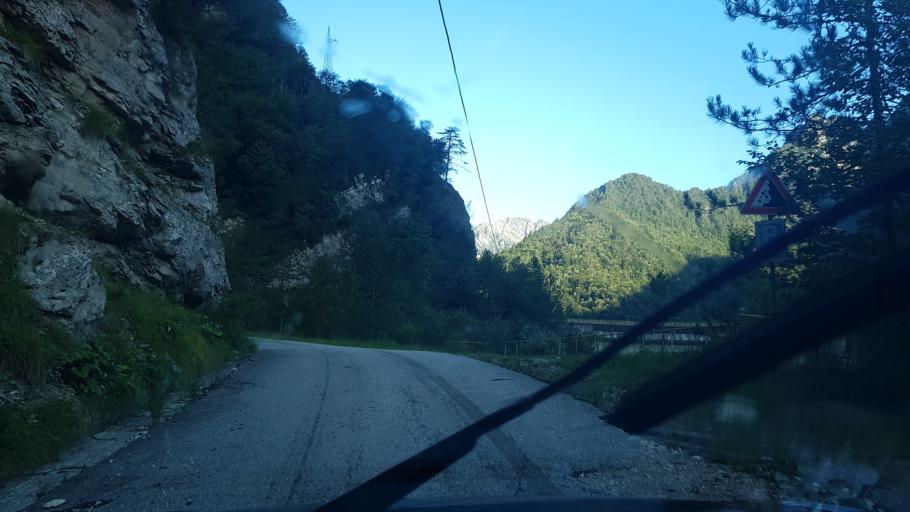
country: IT
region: Friuli Venezia Giulia
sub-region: Provincia di Pordenone
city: Tramonti di Sopra
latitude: 46.2897
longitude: 12.7173
